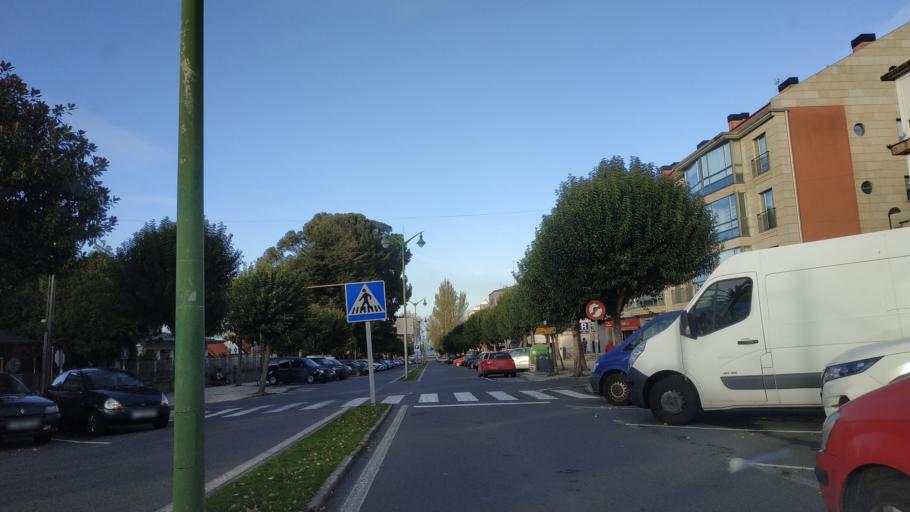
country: ES
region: Galicia
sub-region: Provincia da Coruna
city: A Coruna
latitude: 43.3354
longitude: -8.3779
